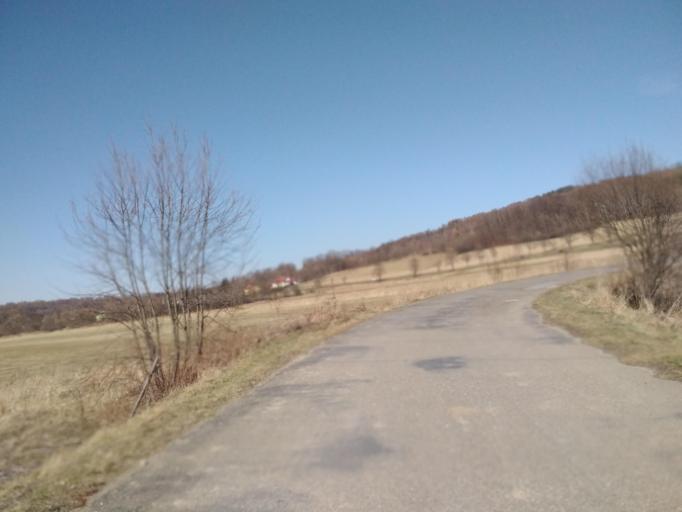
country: PL
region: Subcarpathian Voivodeship
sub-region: Powiat brzozowski
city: Jasienica Rosielna
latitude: 49.7680
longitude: 21.9500
